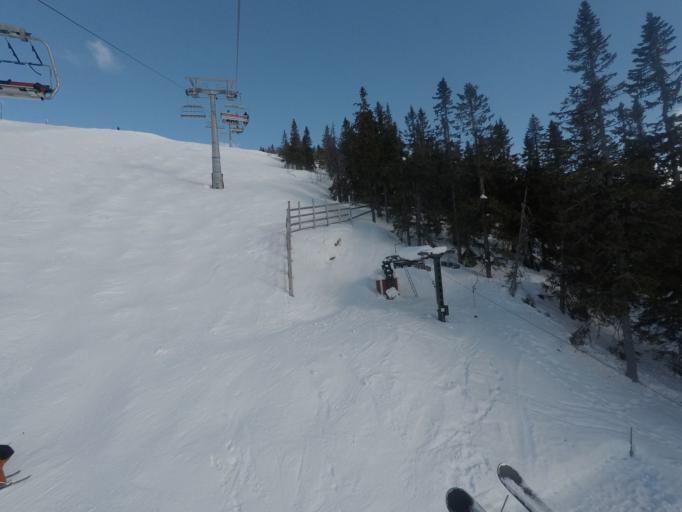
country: NO
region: Hedmark
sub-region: Trysil
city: Innbygda
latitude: 61.1749
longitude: 13.0093
